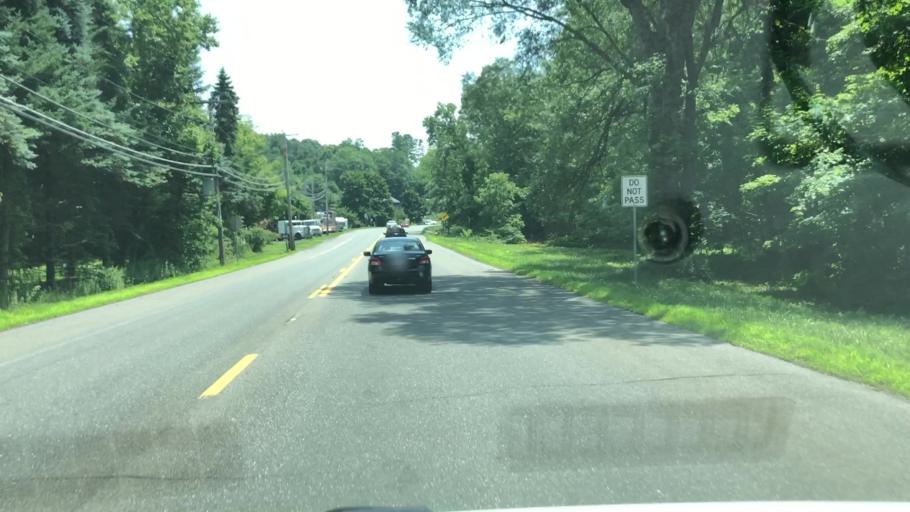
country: US
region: Massachusetts
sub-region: Hampshire County
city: Williamsburg
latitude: 42.3888
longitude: -72.7196
